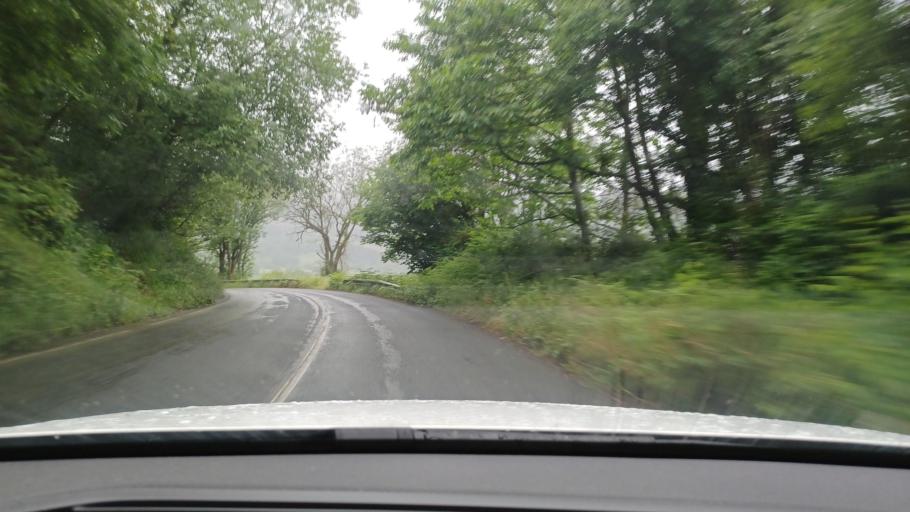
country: ES
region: Asturias
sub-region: Province of Asturias
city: Castandiello
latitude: 43.3091
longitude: -5.8920
